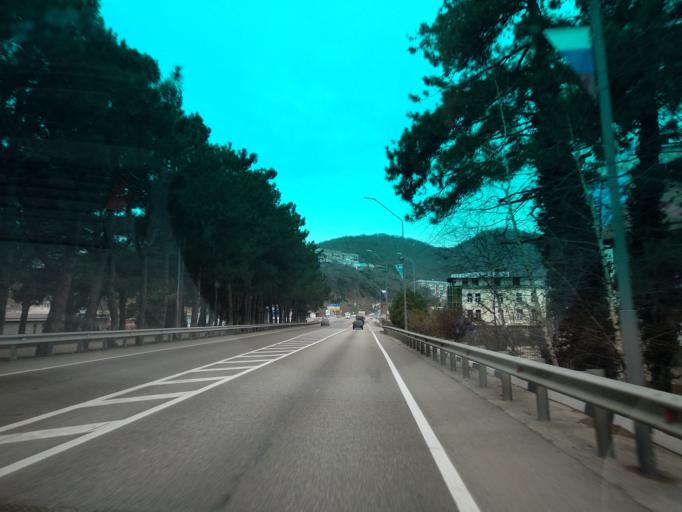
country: RU
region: Krasnodarskiy
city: Ol'ginka
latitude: 44.1979
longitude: 38.8903
